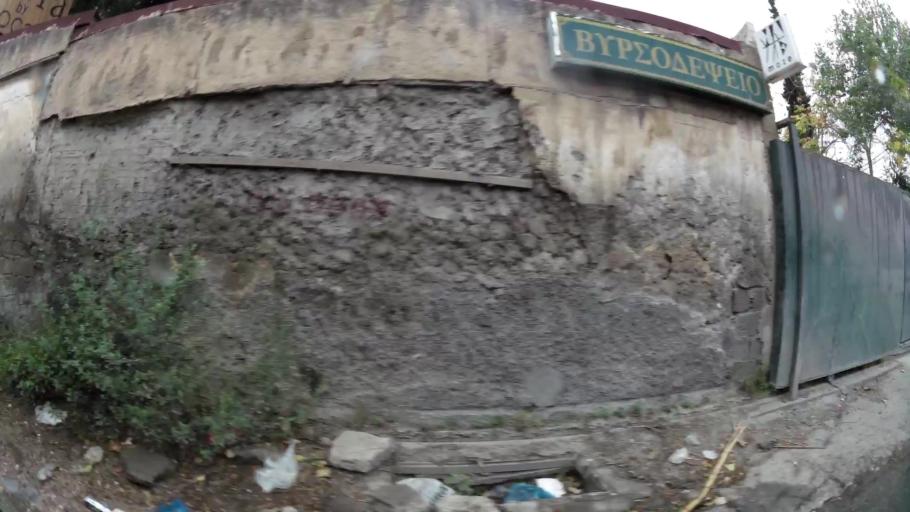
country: GR
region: Attica
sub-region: Nomarchia Athinas
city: Tavros
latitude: 37.9797
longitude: 23.6940
